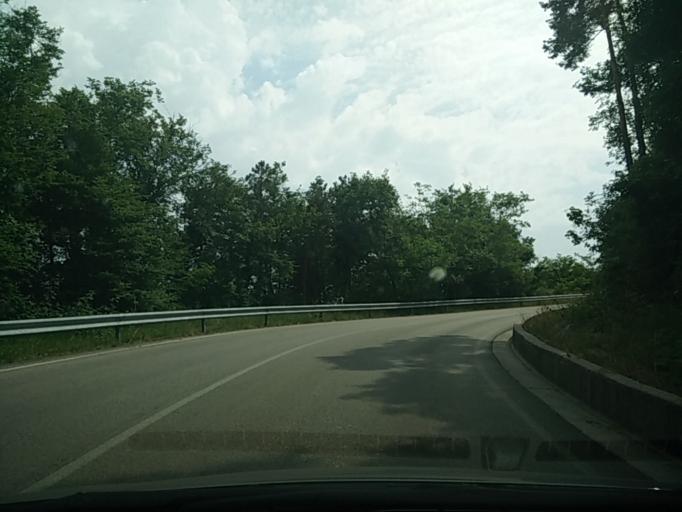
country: IT
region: Friuli Venezia Giulia
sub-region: Provincia di Pordenone
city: Aviano-Castello
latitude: 46.0731
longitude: 12.5636
